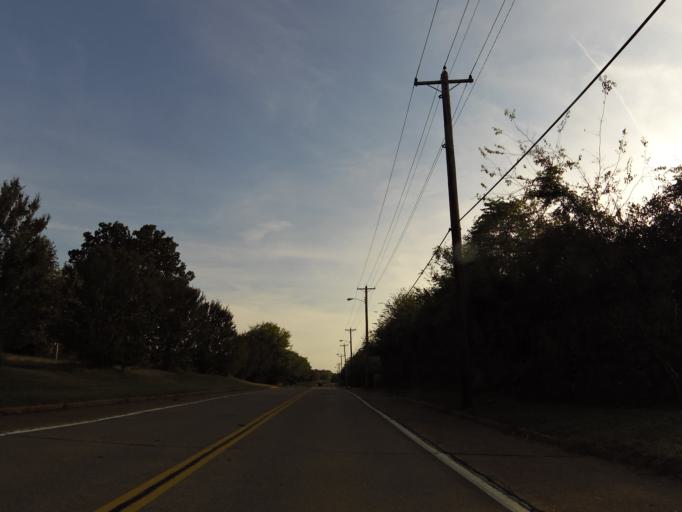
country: US
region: Tennessee
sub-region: Blount County
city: Alcoa
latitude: 35.7748
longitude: -83.9668
